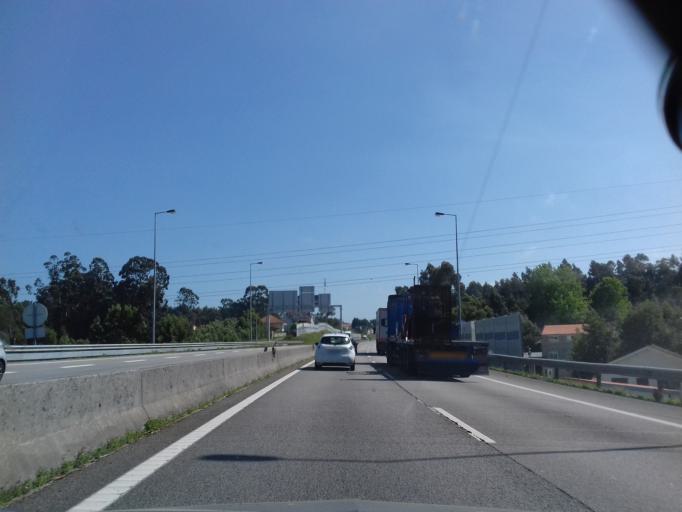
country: PT
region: Aveiro
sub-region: Espinho
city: Silvalde
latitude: 41.0057
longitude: -8.6189
